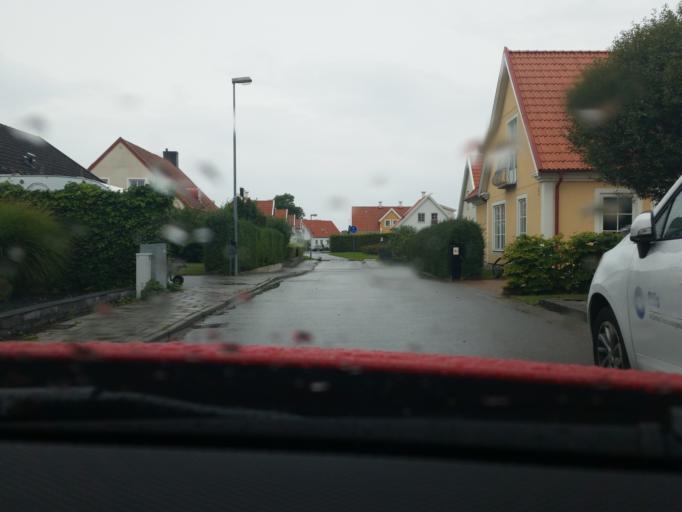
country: SE
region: Skane
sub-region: Malmo
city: Bunkeflostrand
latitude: 55.5304
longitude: 12.9285
